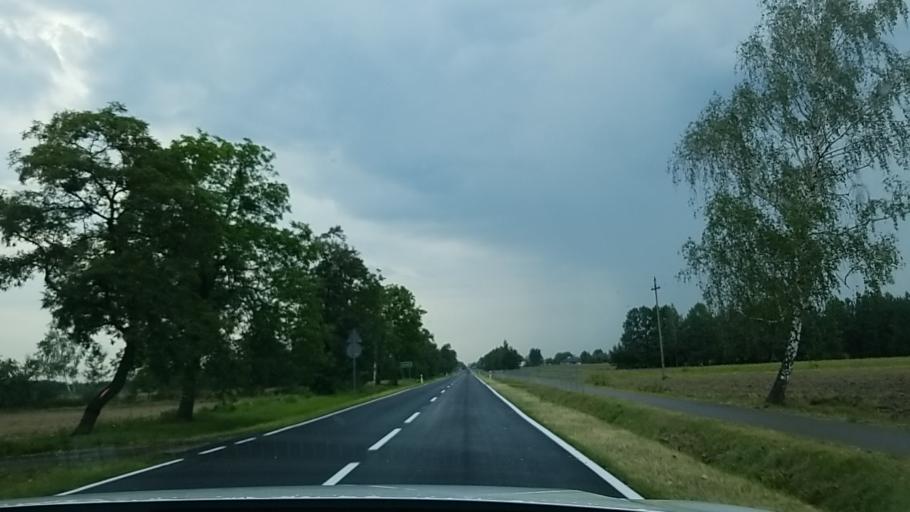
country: PL
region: Lublin Voivodeship
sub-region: Powiat wlodawski
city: Wlodawa
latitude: 51.5797
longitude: 23.5431
